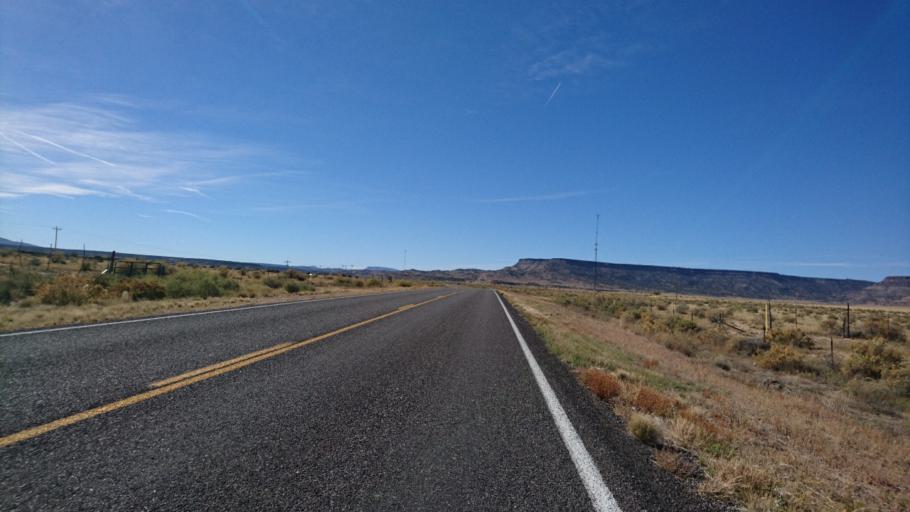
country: US
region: New Mexico
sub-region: Cibola County
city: Skyline-Ganipa
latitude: 35.0825
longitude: -107.6252
